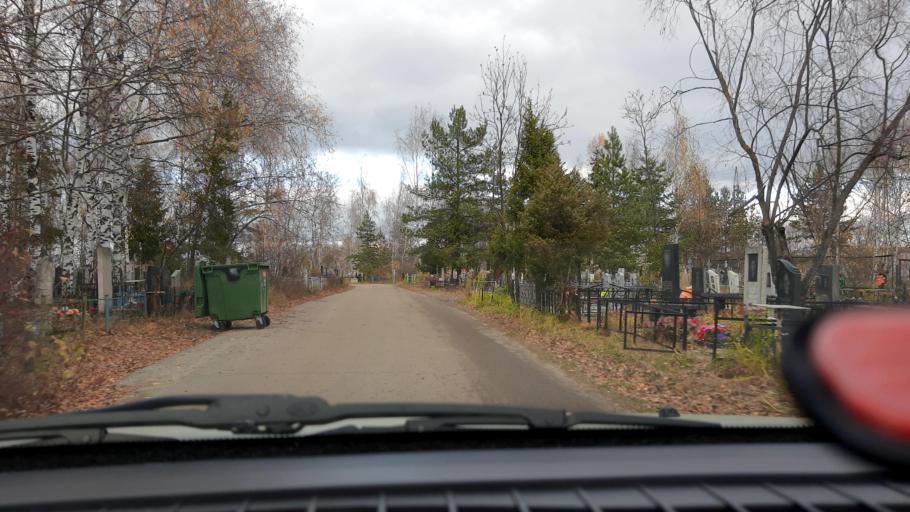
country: RU
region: Nizjnij Novgorod
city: Gorbatovka
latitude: 56.3600
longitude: 43.7875
